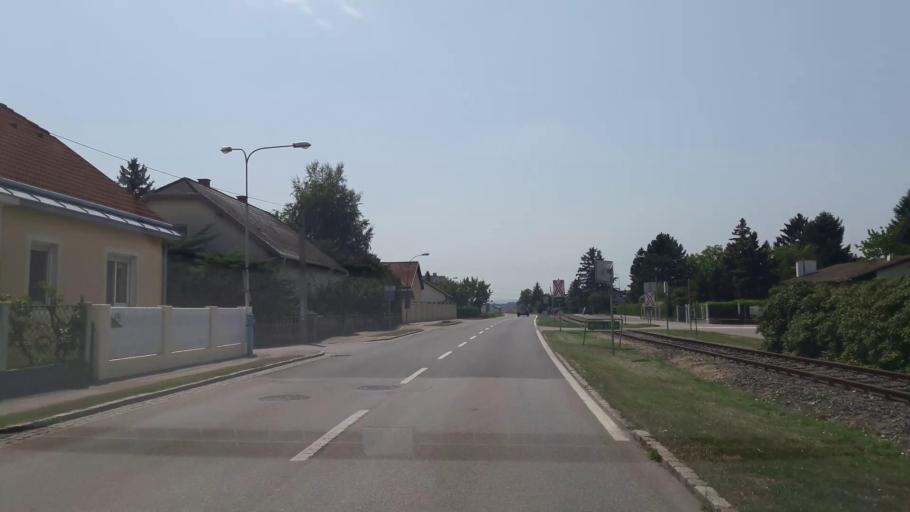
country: AT
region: Lower Austria
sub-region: Politischer Bezirk Bruck an der Leitha
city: Gotzendorf an der Leitha
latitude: 48.0409
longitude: 16.6038
